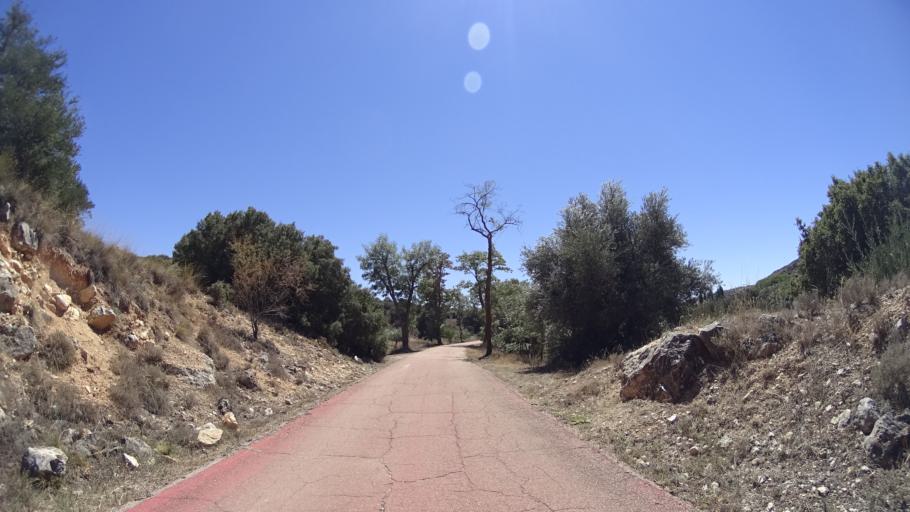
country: ES
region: Madrid
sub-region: Provincia de Madrid
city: Ambite
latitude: 40.3007
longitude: -3.1928
